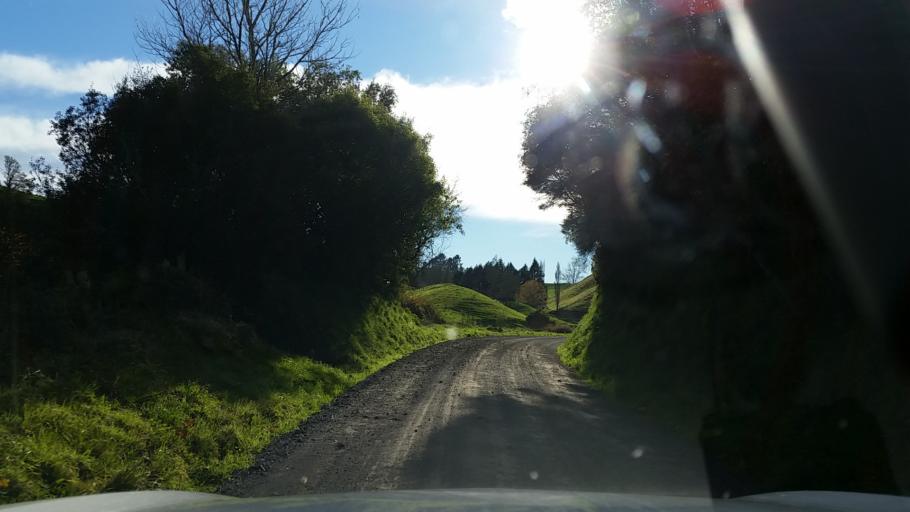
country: NZ
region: Waikato
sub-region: South Waikato District
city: Tokoroa
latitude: -38.3713
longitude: 176.0865
